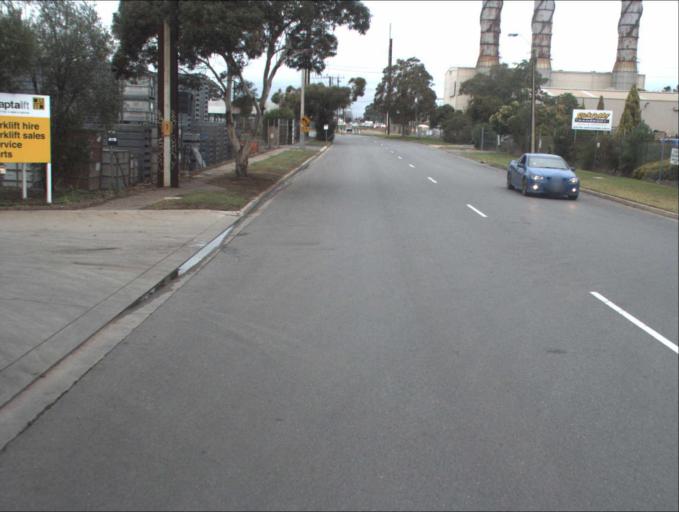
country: AU
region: South Australia
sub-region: Port Adelaide Enfield
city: Blair Athol
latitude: -34.8454
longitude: 138.5822
